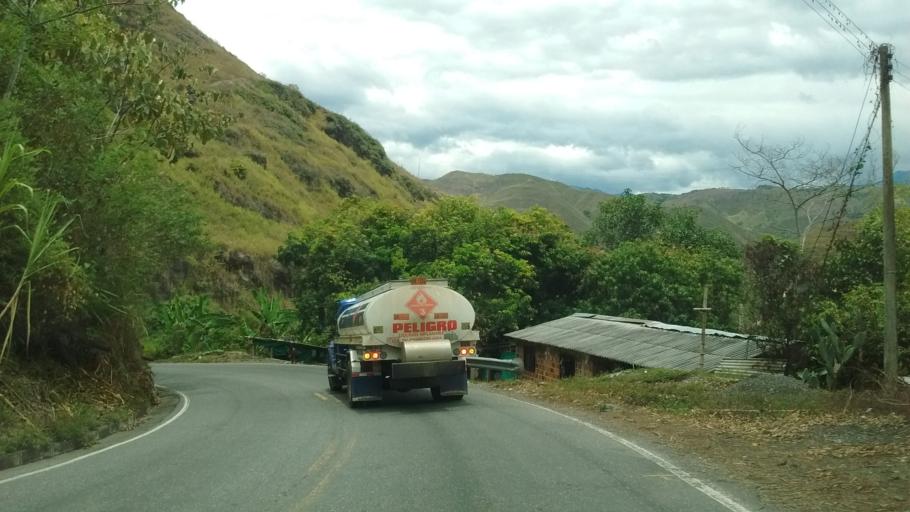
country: CO
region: Cauca
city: La Sierra
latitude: 2.1997
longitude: -76.8254
